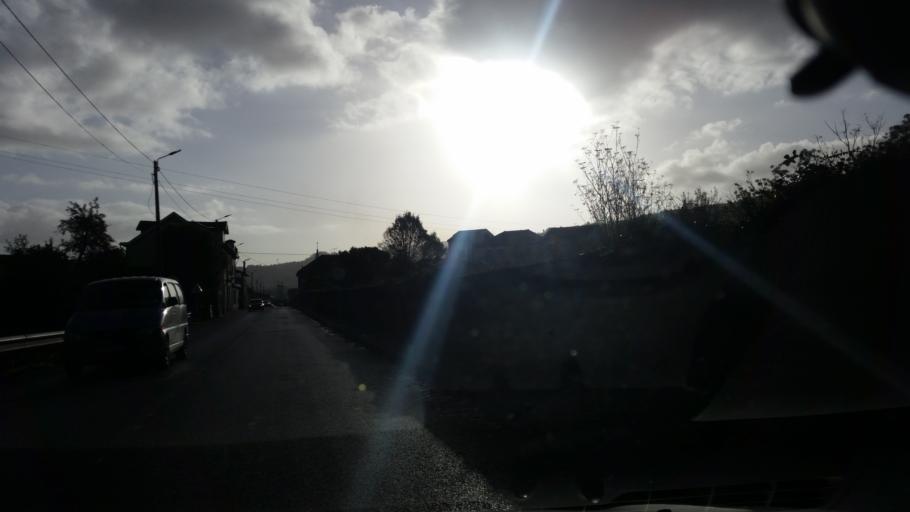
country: PT
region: Porto
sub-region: Santo Tirso
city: Aves
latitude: 41.3578
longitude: -8.4353
